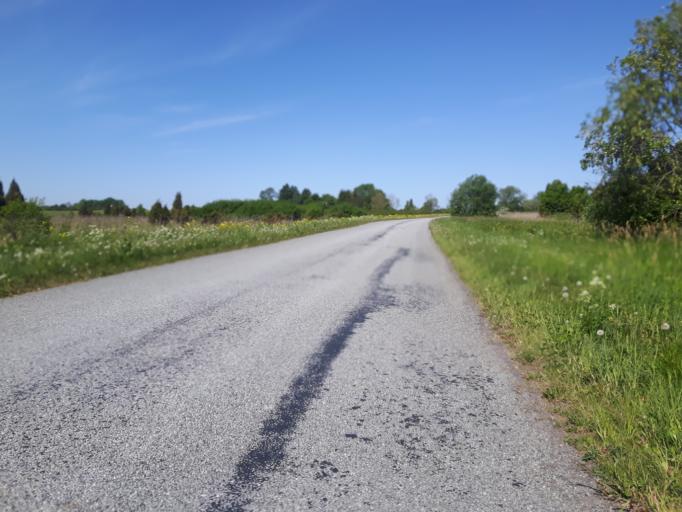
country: EE
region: Ida-Virumaa
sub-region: Aseri vald
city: Aseri
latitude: 59.4634
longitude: 26.8262
